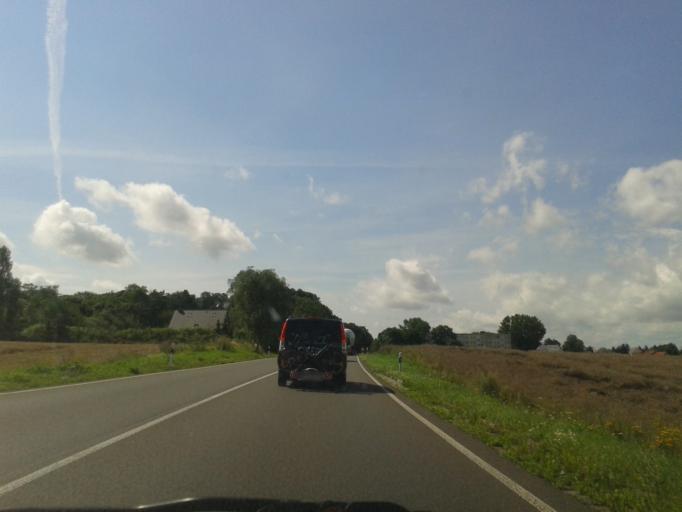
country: DE
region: Mecklenburg-Vorpommern
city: Pasewalk
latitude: 53.4779
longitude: 13.9825
